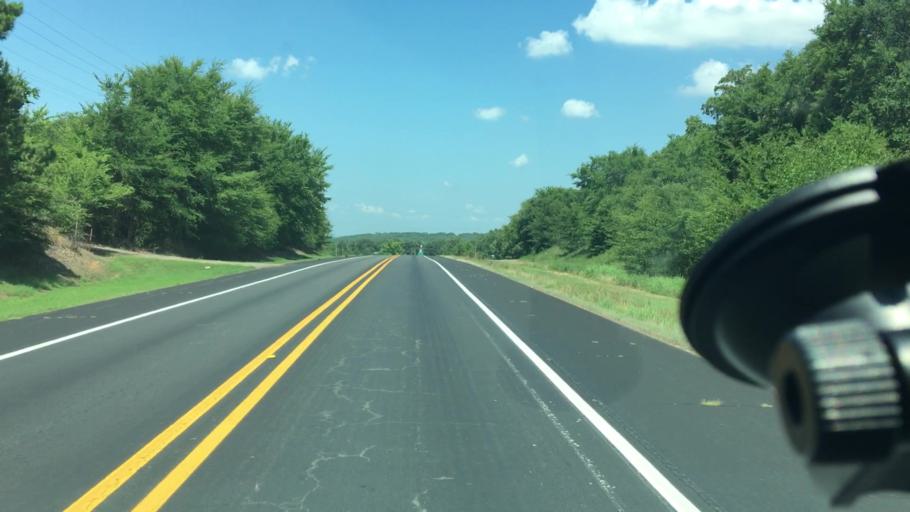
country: US
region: Arkansas
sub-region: Sebastian County
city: Lavaca
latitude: 35.3003
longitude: -94.1589
